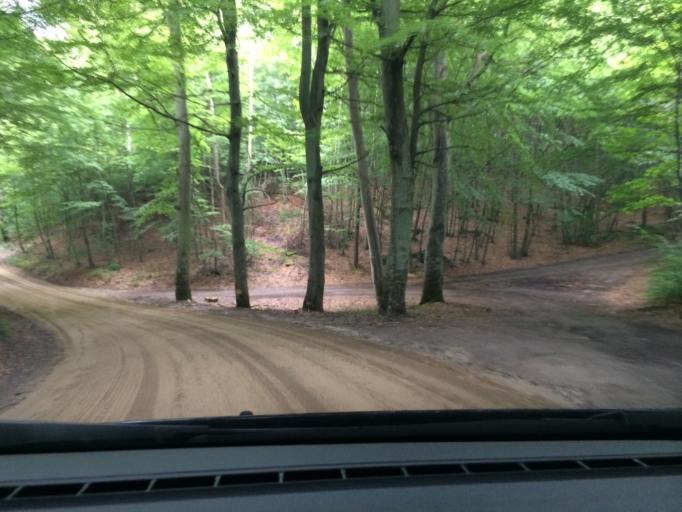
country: DK
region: Zealand
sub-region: Vordingborg Kommune
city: Stege
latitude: 54.9688
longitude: 12.5401
